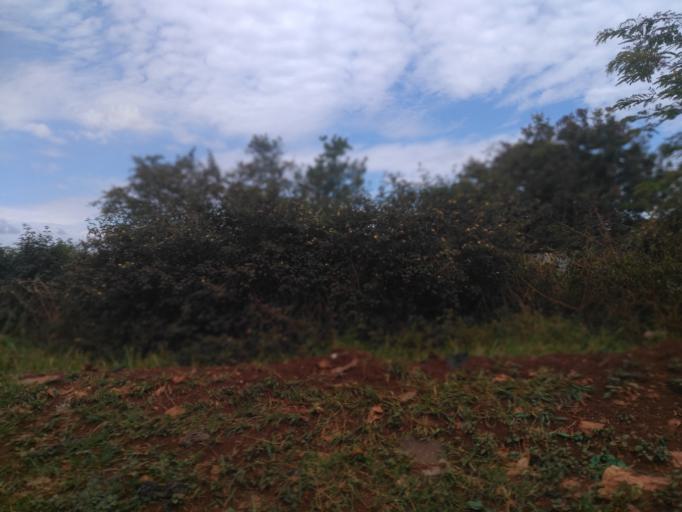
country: UG
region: Central Region
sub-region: Buikwe District
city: Njeru
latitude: 0.4238
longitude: 33.1888
